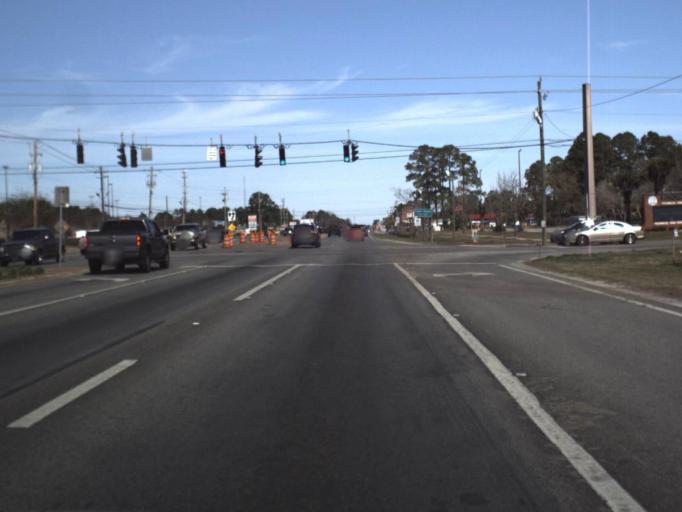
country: US
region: Florida
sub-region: Bay County
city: Hiland Park
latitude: 30.2018
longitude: -85.6496
